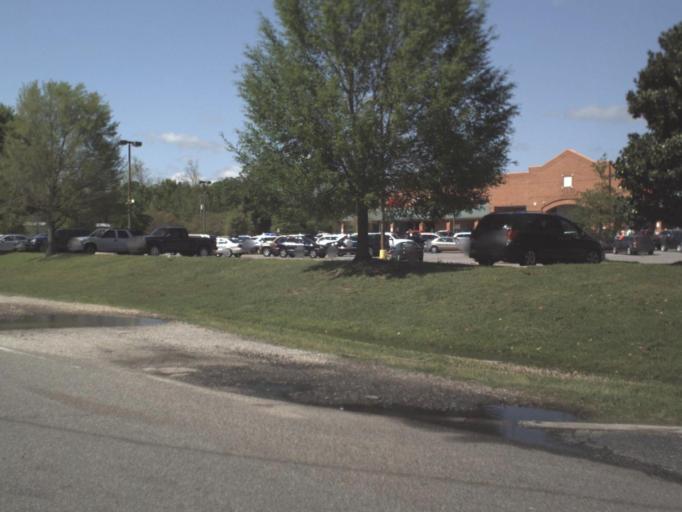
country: US
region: Florida
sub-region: Escambia County
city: Gonzalez
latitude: 30.5795
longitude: -87.2964
